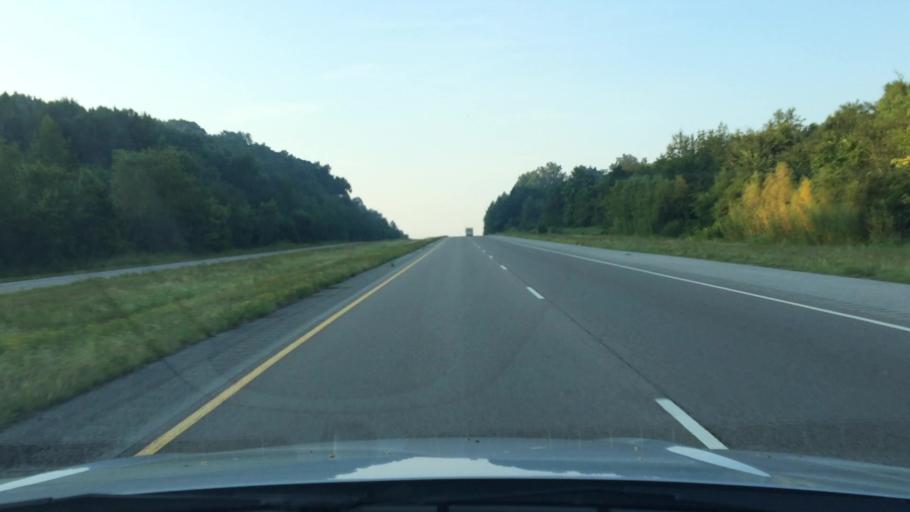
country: US
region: Tennessee
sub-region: Giles County
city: Pulaski
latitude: 35.1826
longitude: -87.0622
